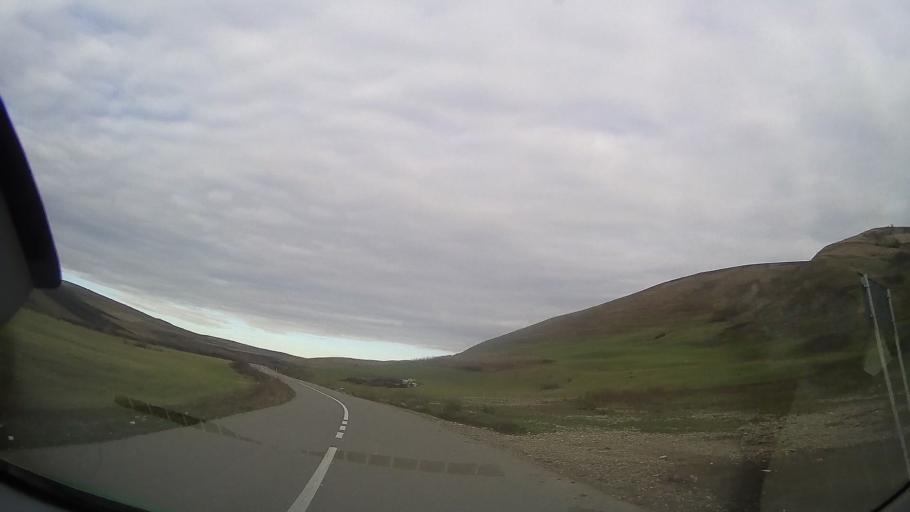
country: RO
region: Bistrita-Nasaud
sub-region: Comuna Silvasu de Campie
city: Silvasu de Campie
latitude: 46.7947
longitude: 24.2961
